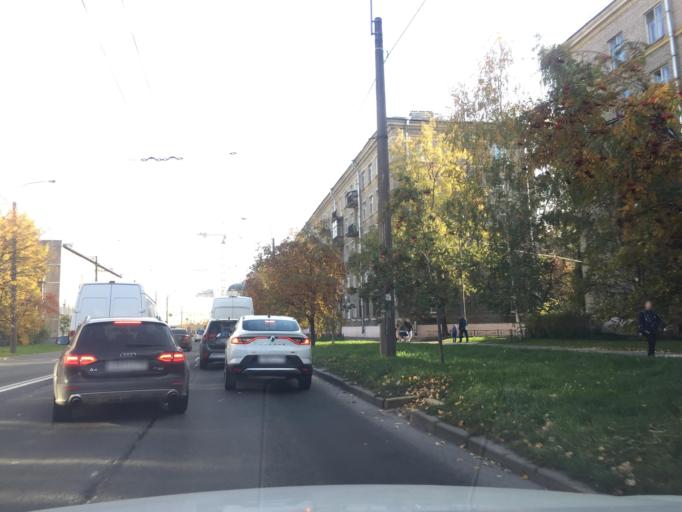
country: RU
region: Leningrad
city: Chernaya Rechka
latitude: 59.9900
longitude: 30.3077
